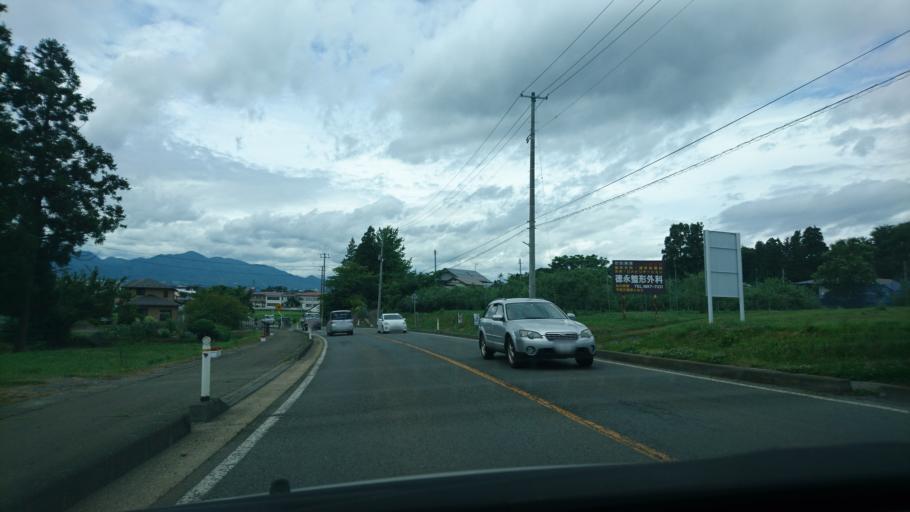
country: JP
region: Iwate
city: Morioka-shi
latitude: 39.6148
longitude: 141.1976
